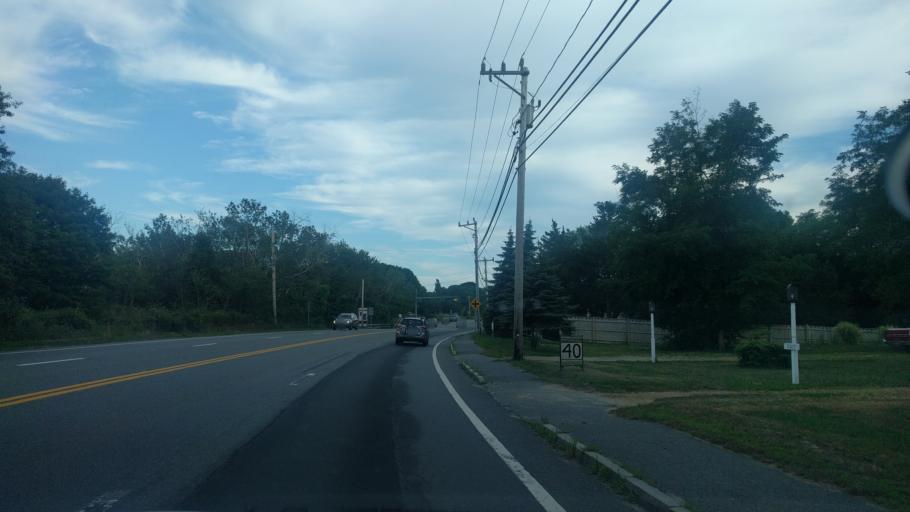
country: US
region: Massachusetts
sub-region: Barnstable County
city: Eastham
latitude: 41.8204
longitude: -69.9698
